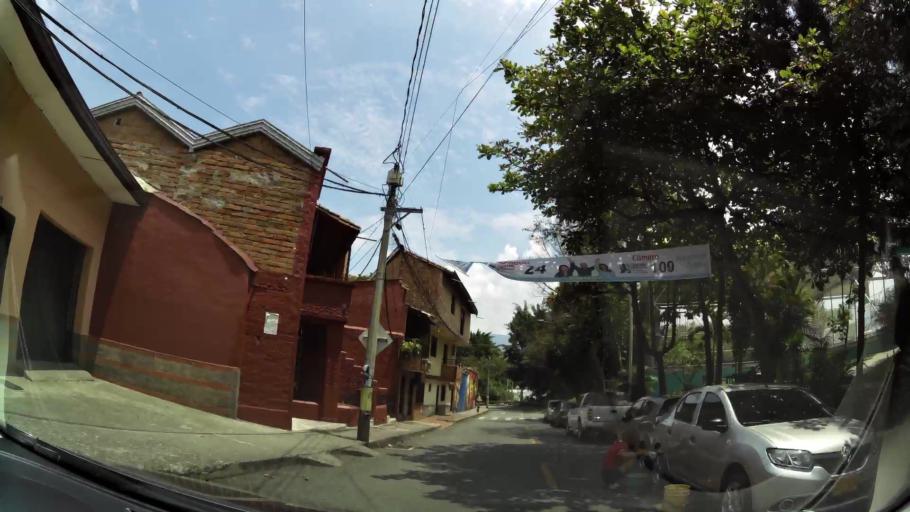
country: CO
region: Antioquia
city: Medellin
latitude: 6.2483
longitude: -75.6090
